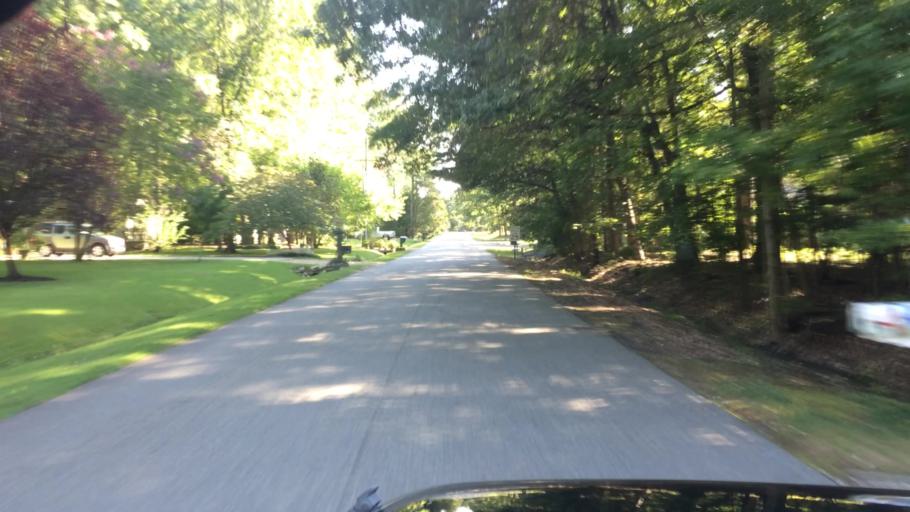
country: US
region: Virginia
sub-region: James City County
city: Williamsburg
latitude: 37.2383
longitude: -76.7972
